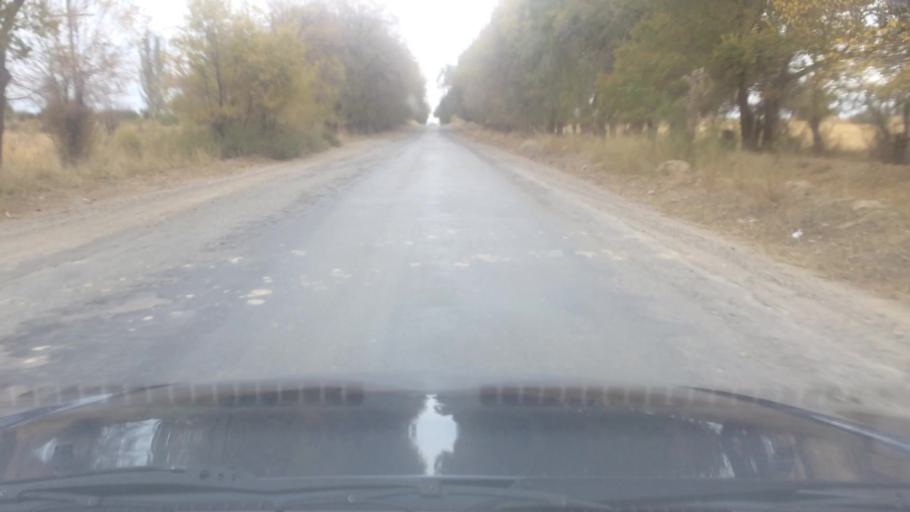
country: KG
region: Ysyk-Koel
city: Balykchy
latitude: 42.3035
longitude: 76.4779
